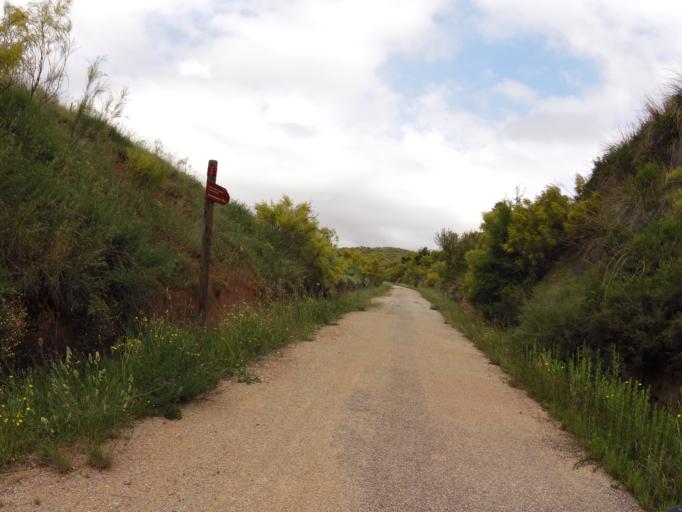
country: ES
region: Castille-La Mancha
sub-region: Provincia de Albacete
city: Alcaraz
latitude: 38.7025
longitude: -2.4903
